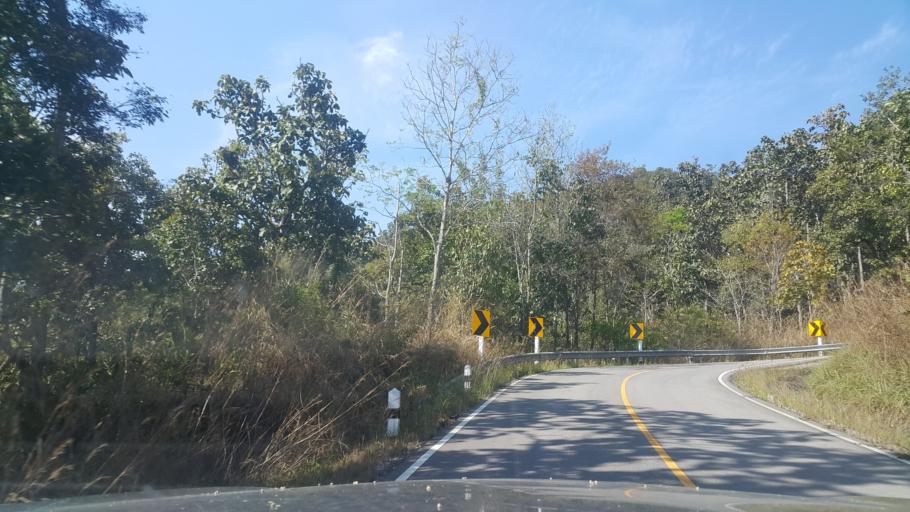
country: TH
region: Chiang Mai
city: Samoeng
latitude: 18.8998
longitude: 98.6764
